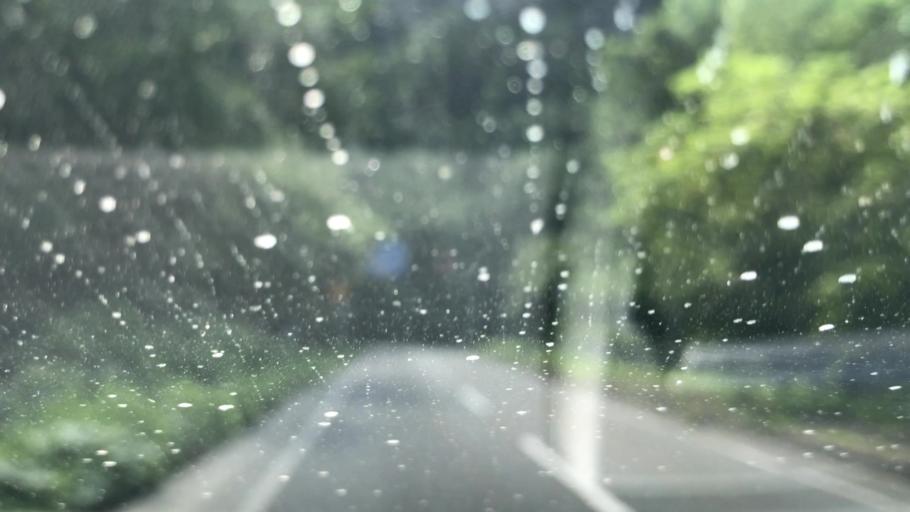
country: JP
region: Hokkaido
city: Shimo-furano
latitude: 42.8505
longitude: 142.4175
